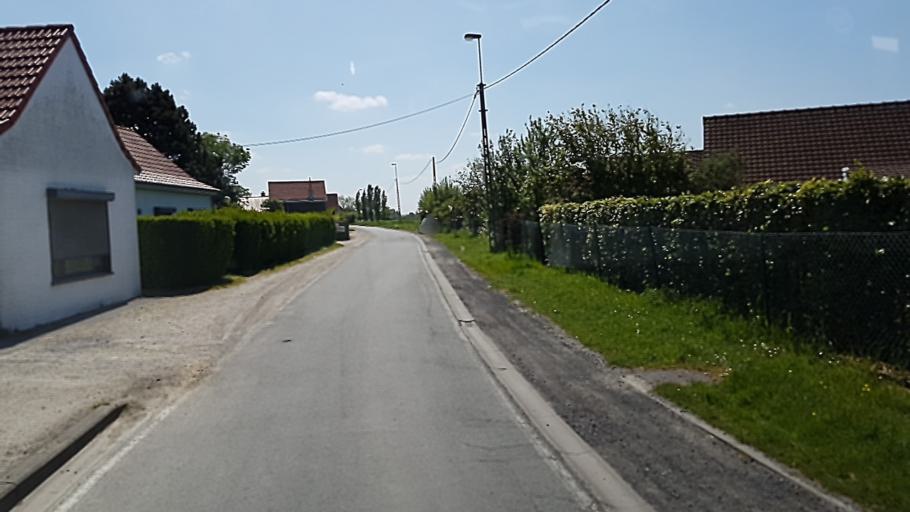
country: BE
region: Flanders
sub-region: Provincie West-Vlaanderen
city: De Haan
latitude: 51.2628
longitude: 3.0380
